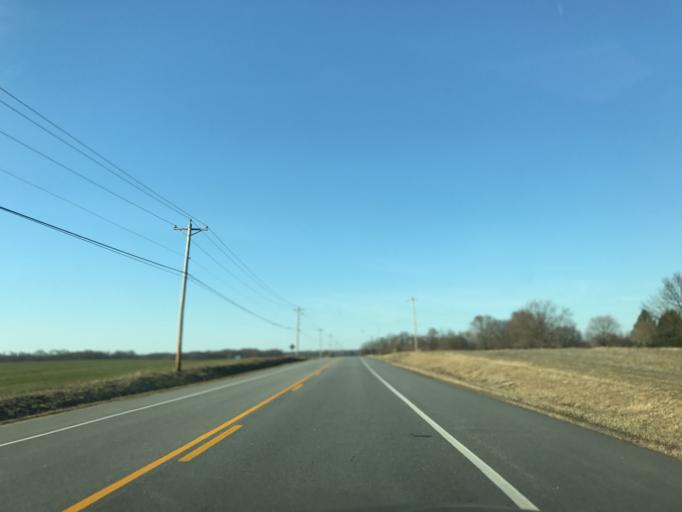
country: US
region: Maryland
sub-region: Queen Anne's County
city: Kingstown
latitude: 39.2134
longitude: -75.8637
